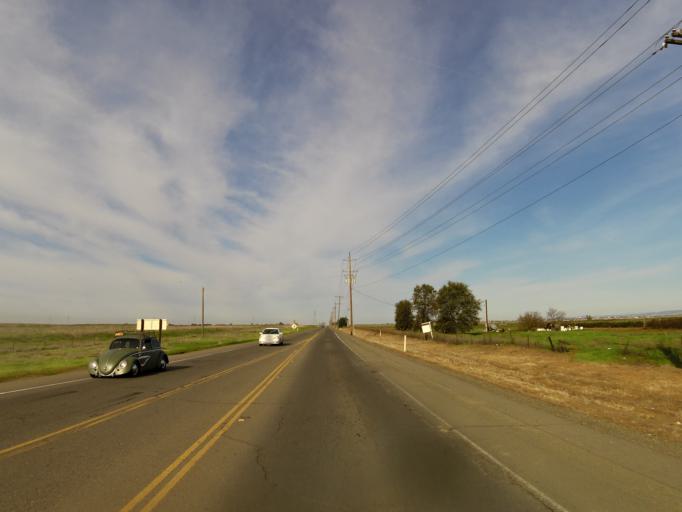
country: US
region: California
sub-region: Sacramento County
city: Wilton
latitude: 38.5069
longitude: -121.2425
